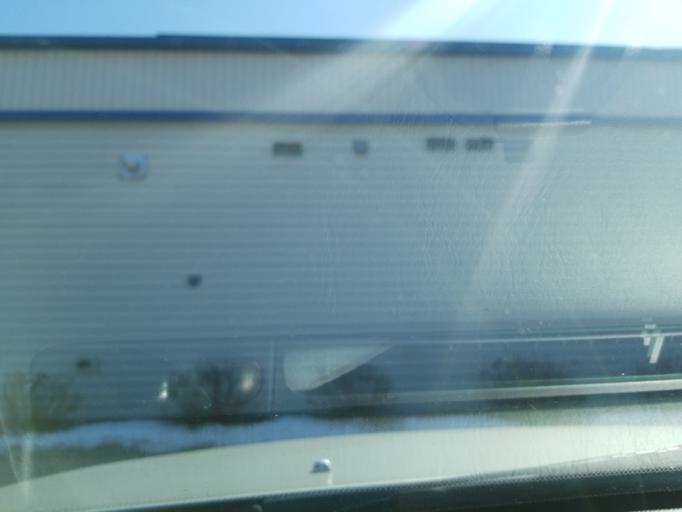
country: US
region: Wisconsin
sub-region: Iowa County
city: Dodgeville
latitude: 42.9721
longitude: -90.1270
